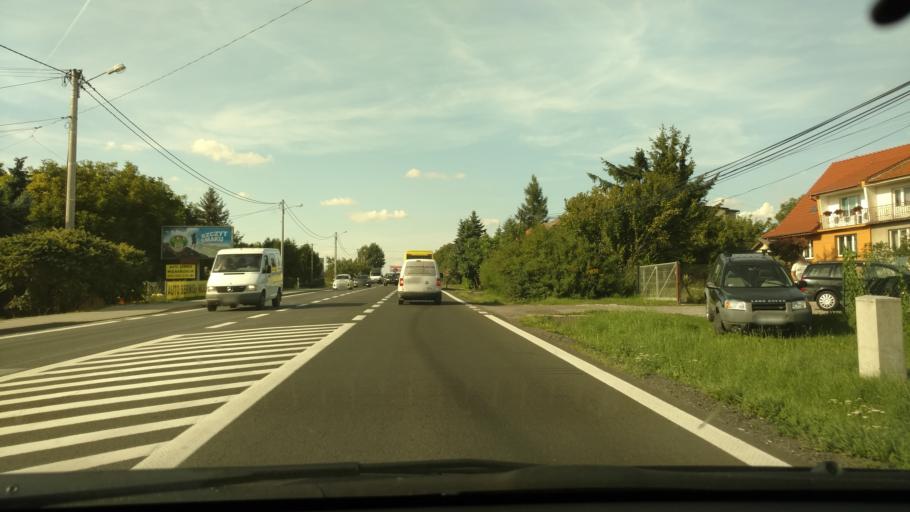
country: PL
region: Lesser Poland Voivodeship
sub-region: Powiat krakowski
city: Michalowice
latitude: 50.1265
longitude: 19.9681
